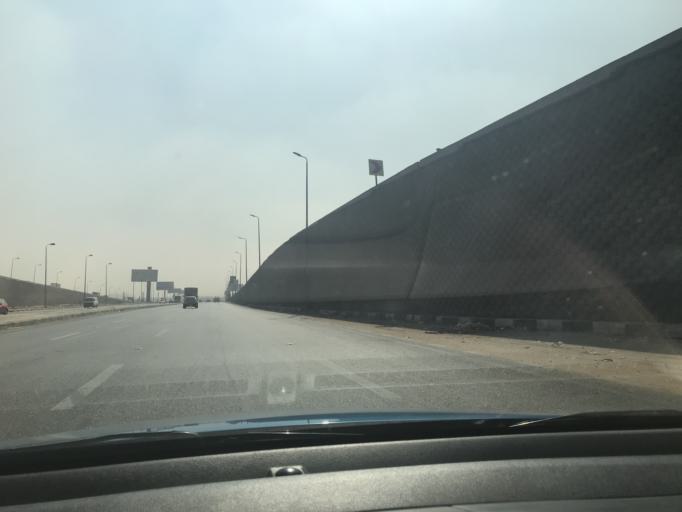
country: EG
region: Muhafazat al Qalyubiyah
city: Al Khankah
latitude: 30.1613
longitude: 31.4701
